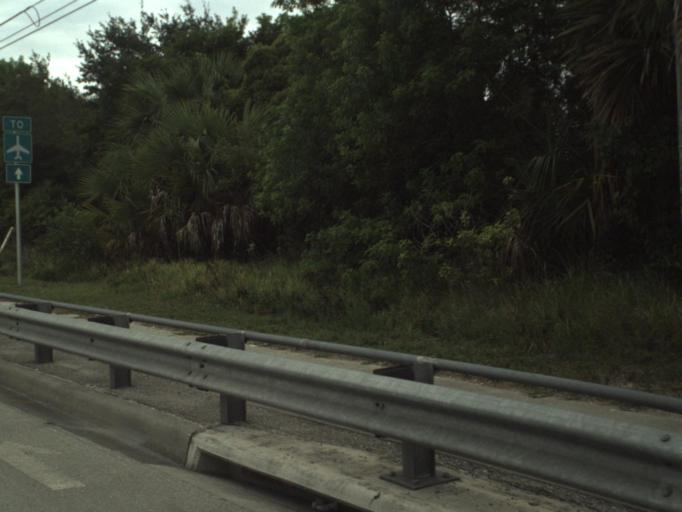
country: US
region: Florida
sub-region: Palm Beach County
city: Royal Palm Beach
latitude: 26.6798
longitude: -80.1872
